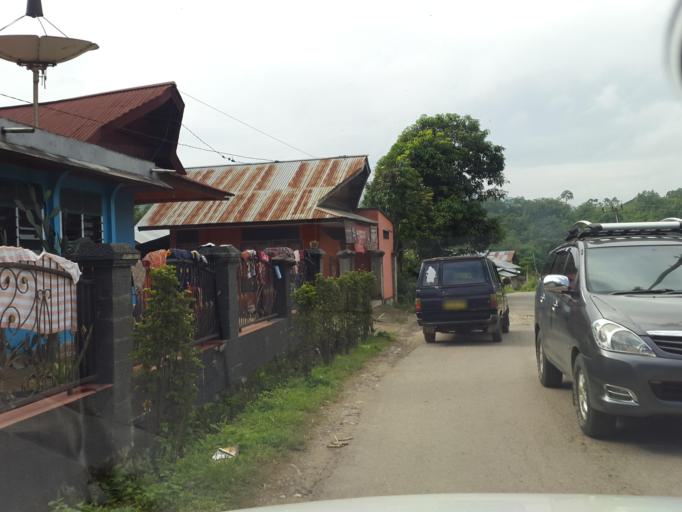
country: ID
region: South Sulawesi
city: Rantepao
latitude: -3.0119
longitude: 119.8655
